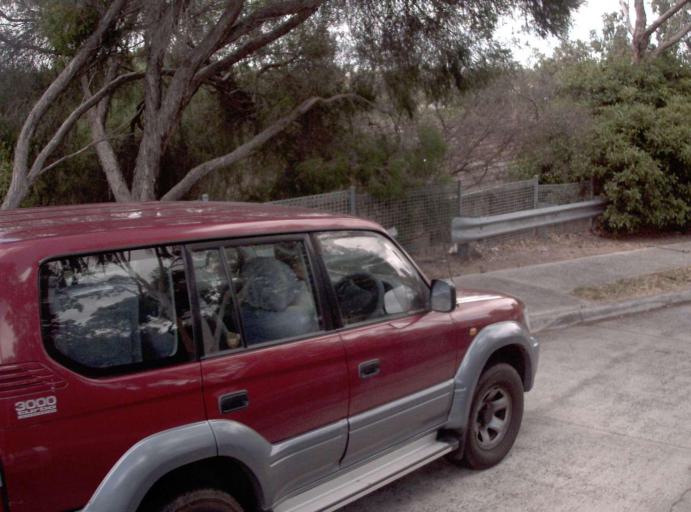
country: AU
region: Victoria
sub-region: Monash
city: Notting Hill
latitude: -37.8859
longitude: 145.1319
